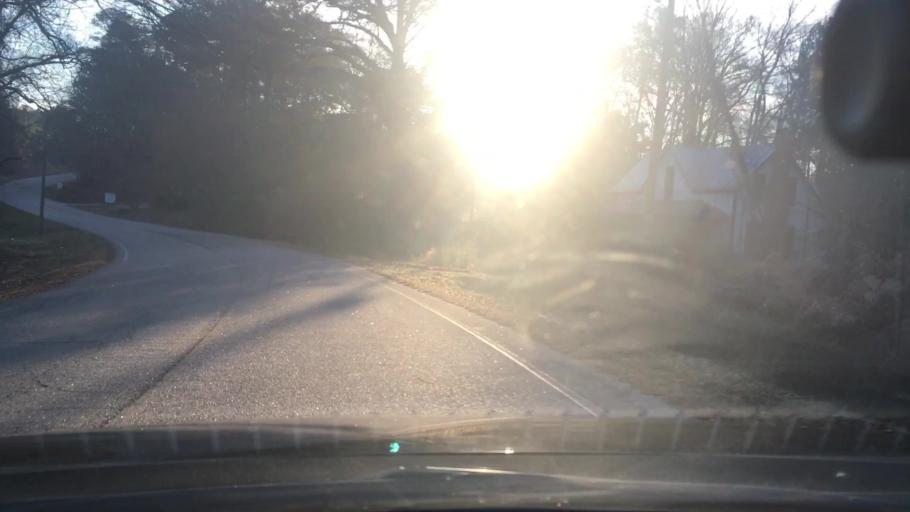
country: US
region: Georgia
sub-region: Coweta County
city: Senoia
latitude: 33.2889
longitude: -84.4570
